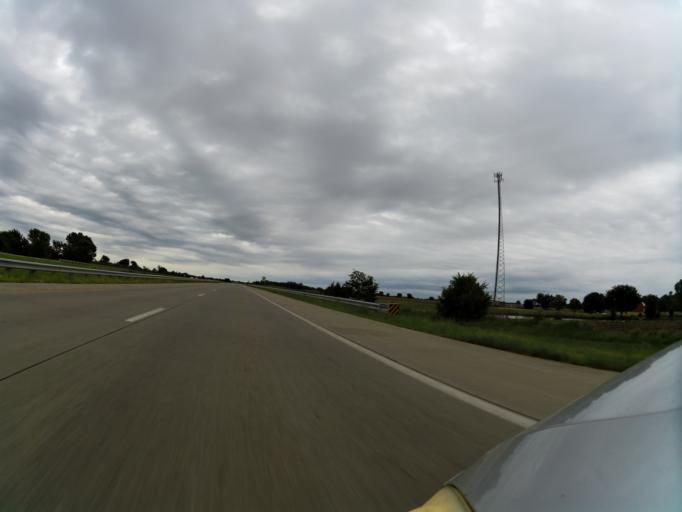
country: US
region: Kansas
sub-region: Reno County
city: Haven
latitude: 37.8943
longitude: -97.7732
